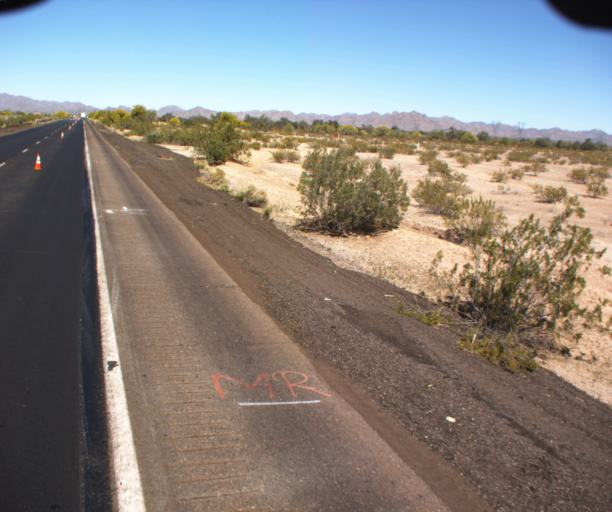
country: US
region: Arizona
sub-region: Maricopa County
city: Gila Bend
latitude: 33.0088
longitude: -112.6549
